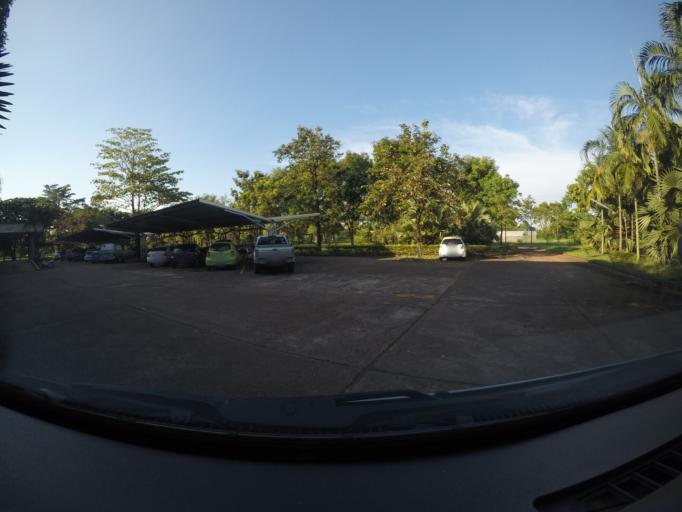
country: TH
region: Sakon Nakhon
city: Sakon Nakhon
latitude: 17.2959
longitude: 104.1162
